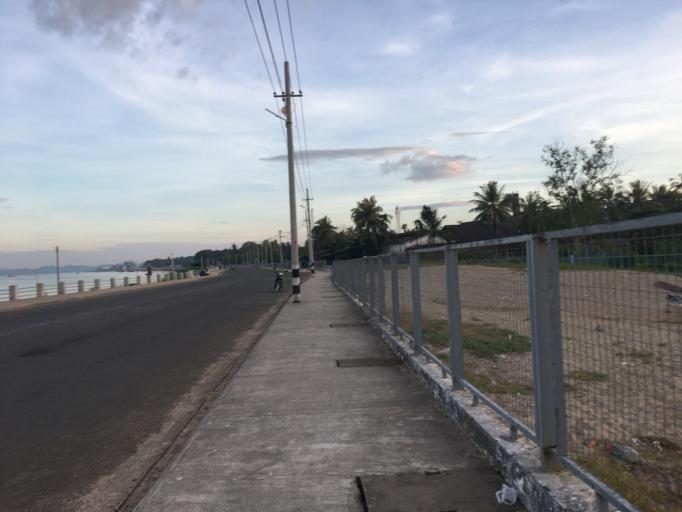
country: MM
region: Mon
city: Mawlamyine
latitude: 16.4542
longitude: 97.6233
